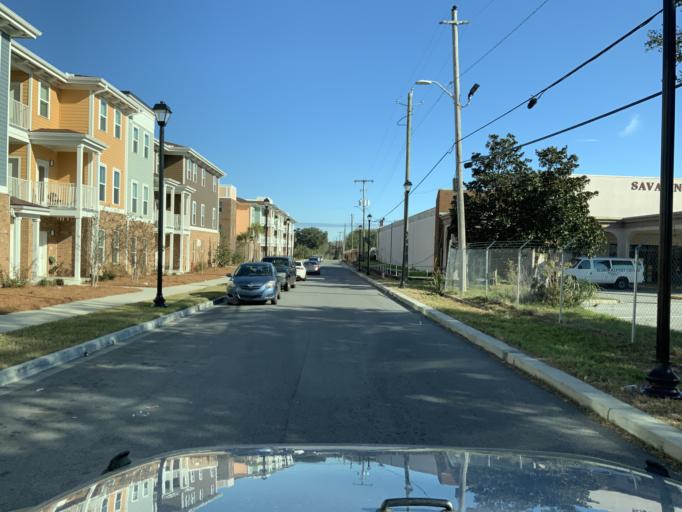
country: US
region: Georgia
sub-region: Chatham County
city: Savannah
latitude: 32.0726
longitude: -81.0834
